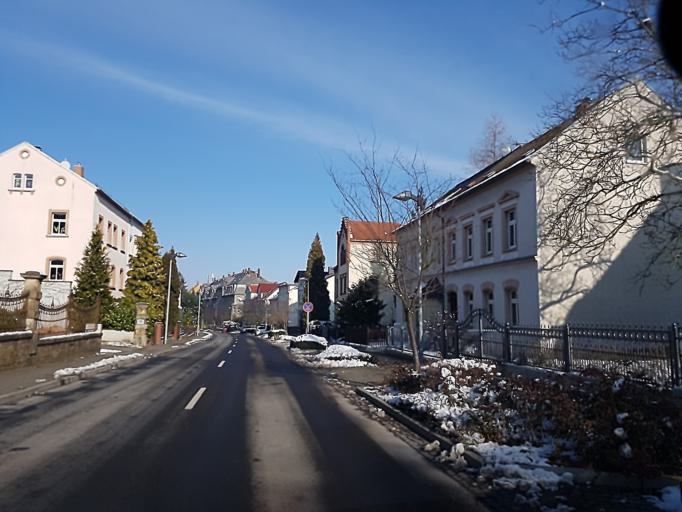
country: DE
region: Saxony
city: Leisnig
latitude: 51.1541
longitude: 12.9276
